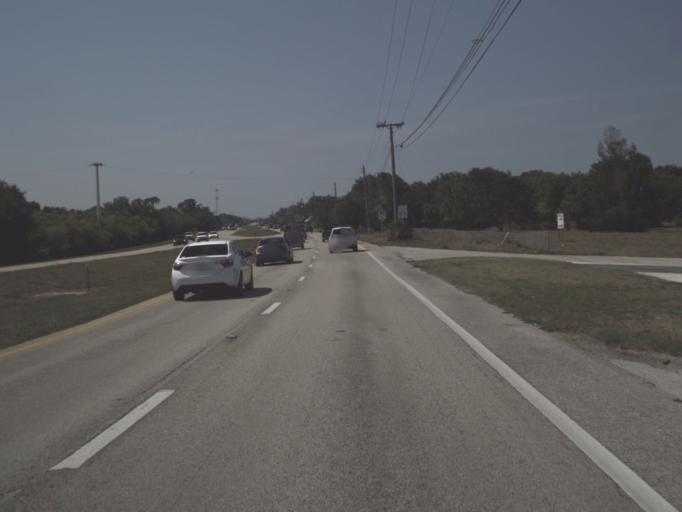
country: US
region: Florida
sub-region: Brevard County
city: Rockledge
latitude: 28.2977
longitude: -80.7011
